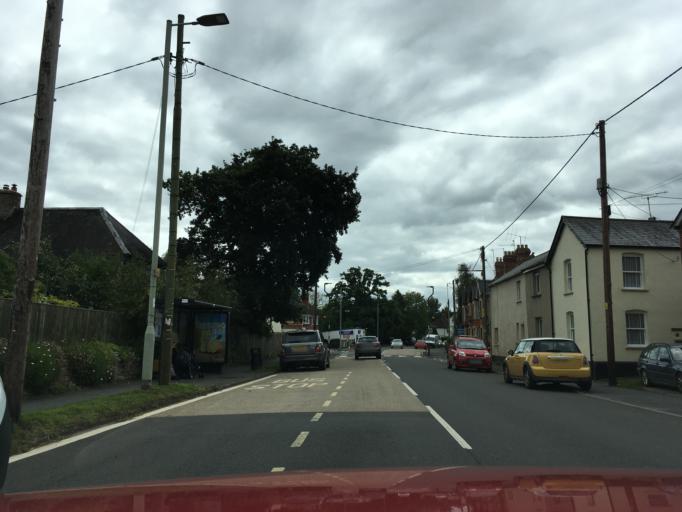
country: GB
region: England
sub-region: Devon
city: Cullompton
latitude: 50.8518
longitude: -3.3943
